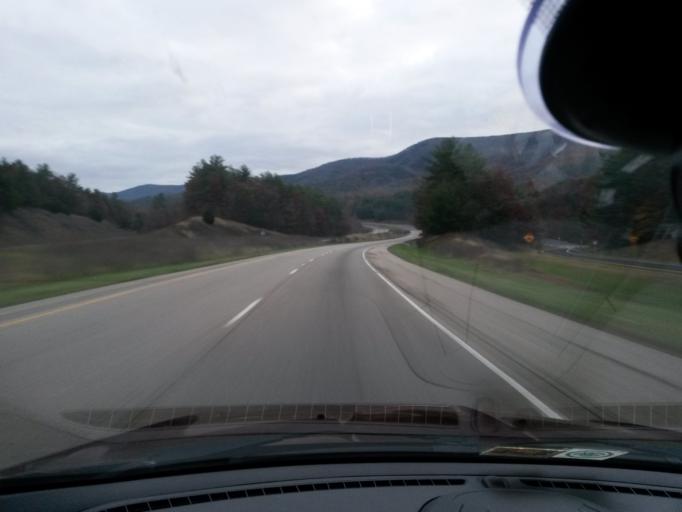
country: US
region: Virginia
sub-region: Alleghany County
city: Clifton Forge
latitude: 37.8130
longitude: -79.6804
